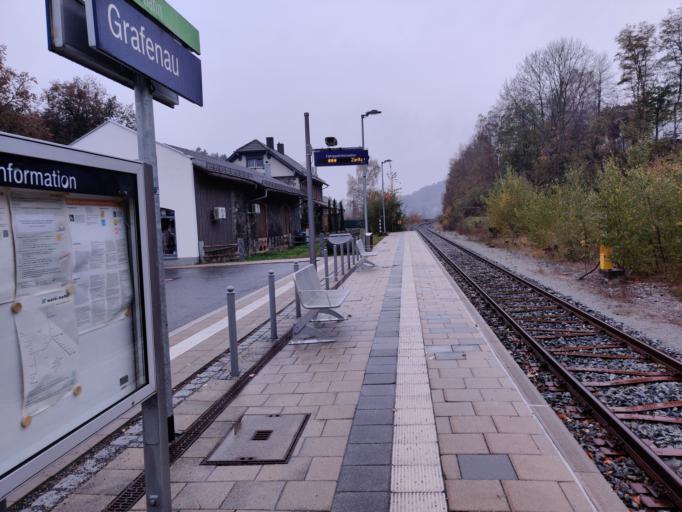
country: DE
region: Bavaria
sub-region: Lower Bavaria
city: Grafenau
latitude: 48.8561
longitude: 13.3938
